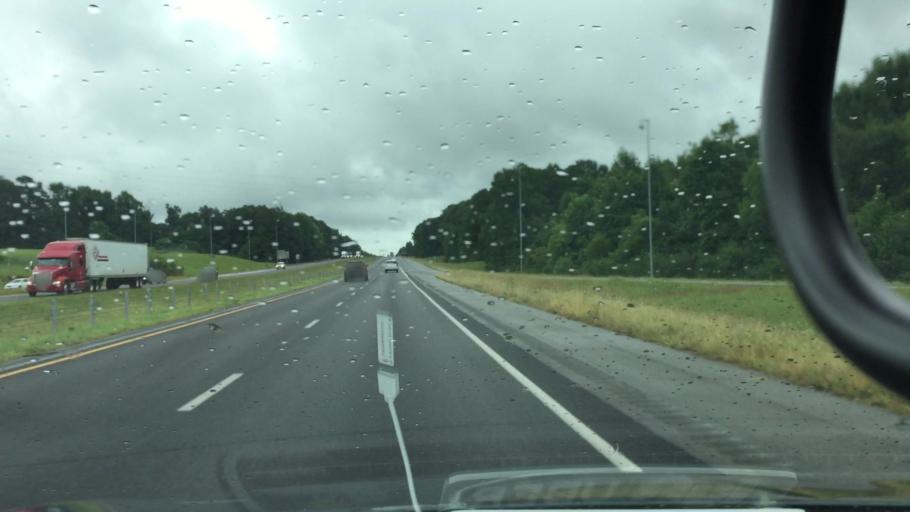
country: US
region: Alabama
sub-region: Lee County
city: Opelika
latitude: 32.6176
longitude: -85.3996
